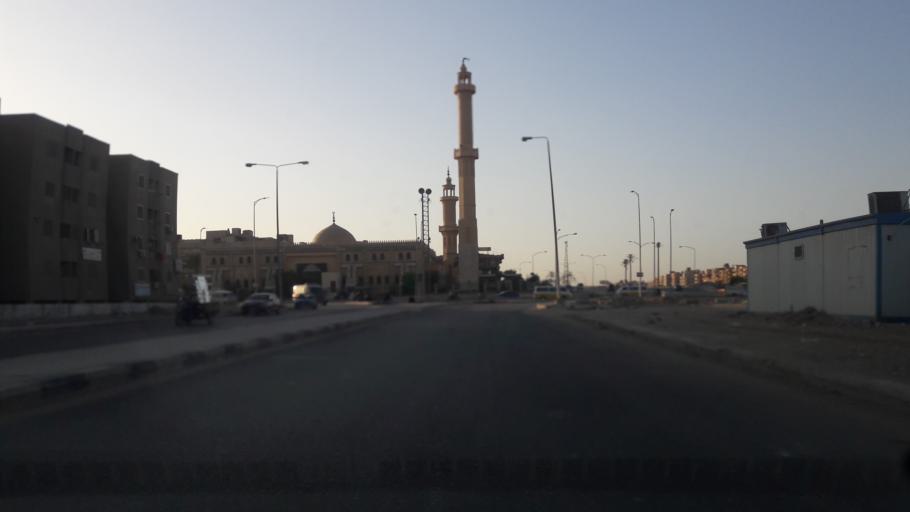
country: EG
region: Al Jizah
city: Madinat Sittah Uktubar
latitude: 29.9516
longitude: 30.9362
